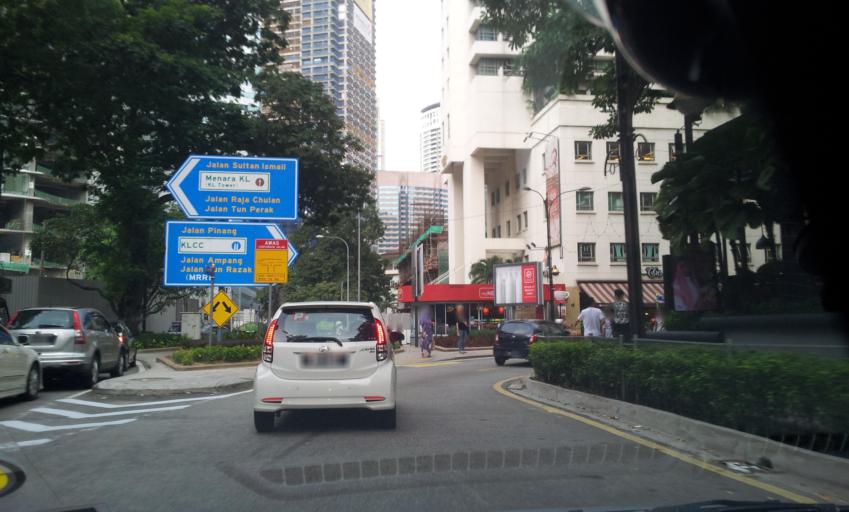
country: MY
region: Kuala Lumpur
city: Kuala Lumpur
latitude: 3.1544
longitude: 101.7087
